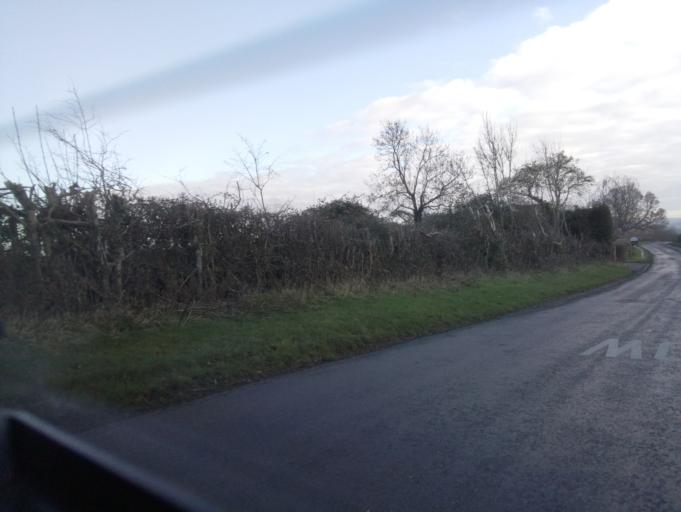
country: GB
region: England
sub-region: Staffordshire
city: Barton under Needwood
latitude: 52.7965
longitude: -1.7106
